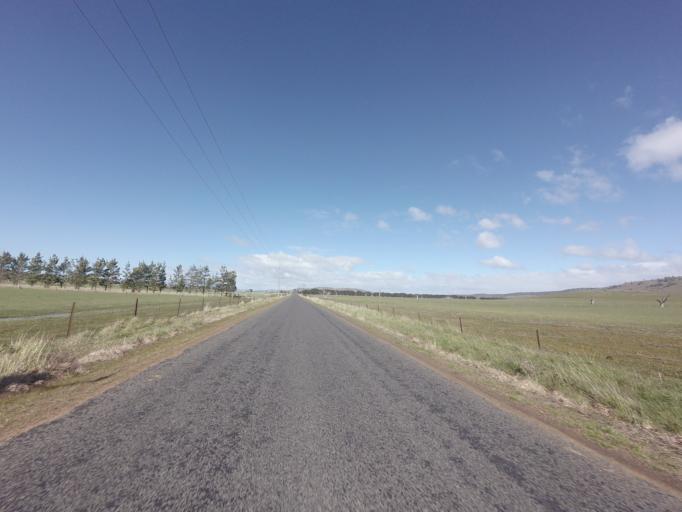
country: AU
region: Tasmania
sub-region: Northern Midlands
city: Evandale
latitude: -41.9877
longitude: 147.4514
